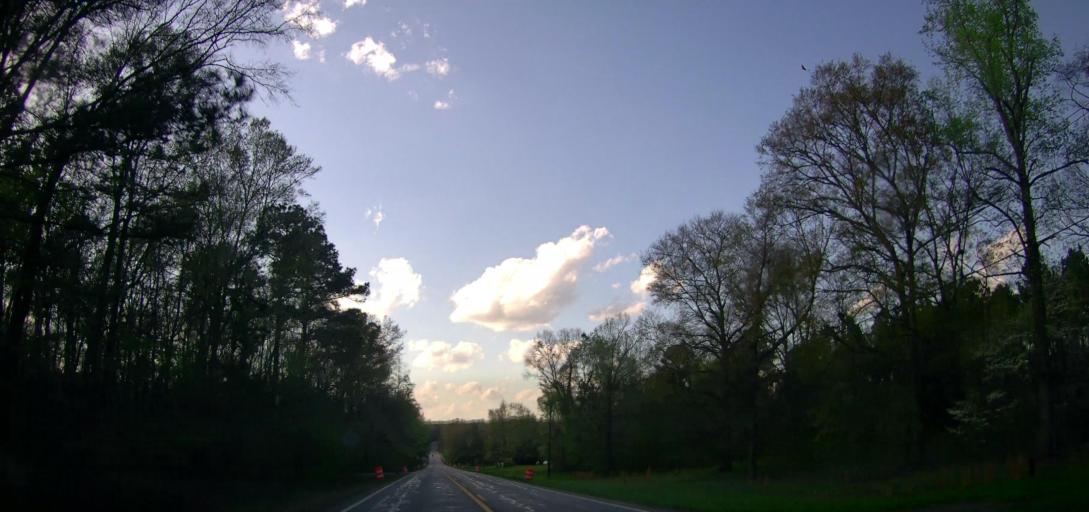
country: US
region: Georgia
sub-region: Putnam County
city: Eatonton
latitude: 33.1783
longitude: -83.4062
